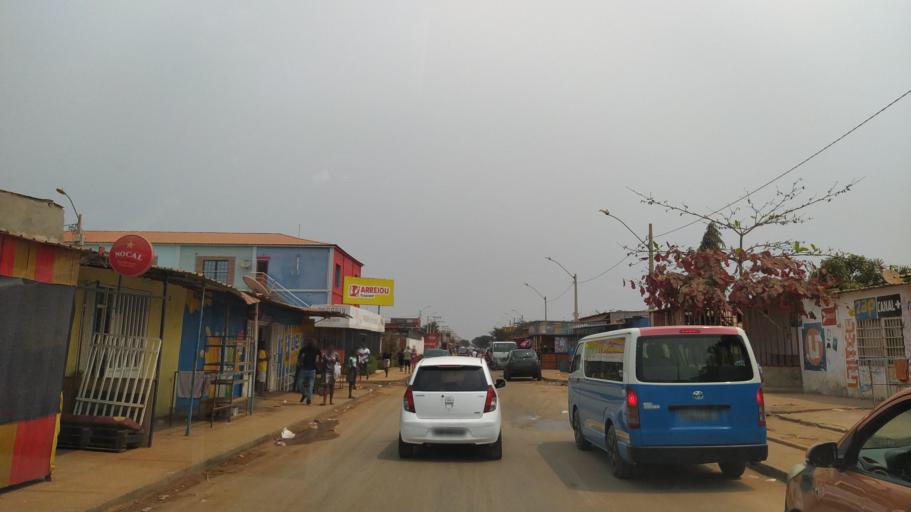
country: AO
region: Luanda
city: Luanda
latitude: -9.0718
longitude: 13.4090
